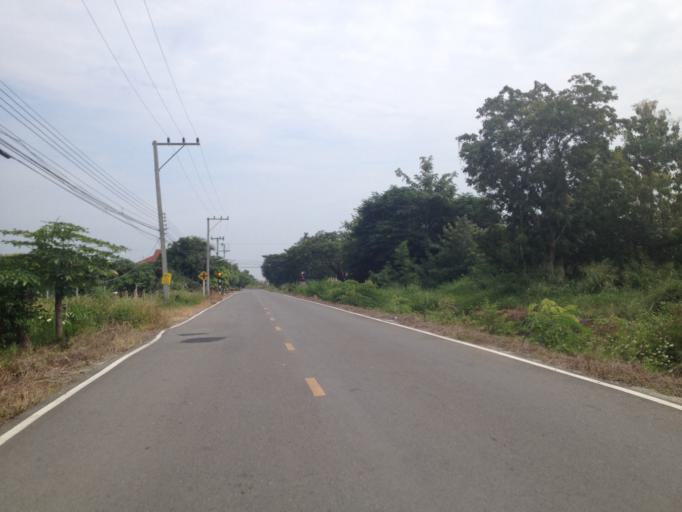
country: TH
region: Chiang Mai
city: San Pa Tong
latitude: 18.6562
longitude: 98.8865
